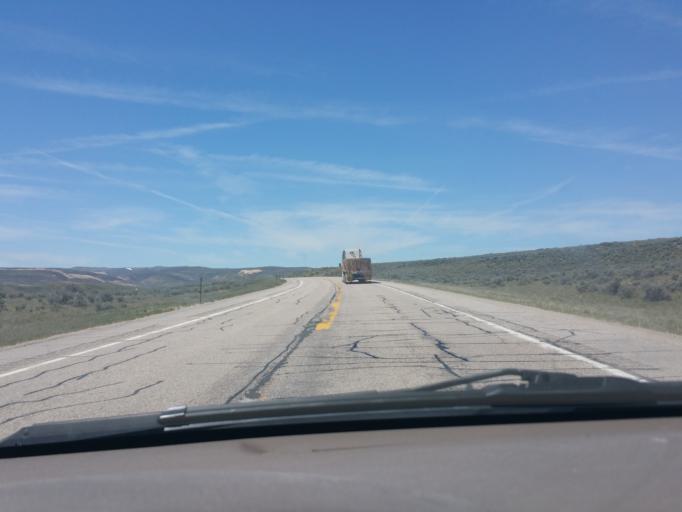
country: US
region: Wyoming
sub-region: Lincoln County
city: Kemmerer
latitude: 41.8152
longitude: -110.6646
